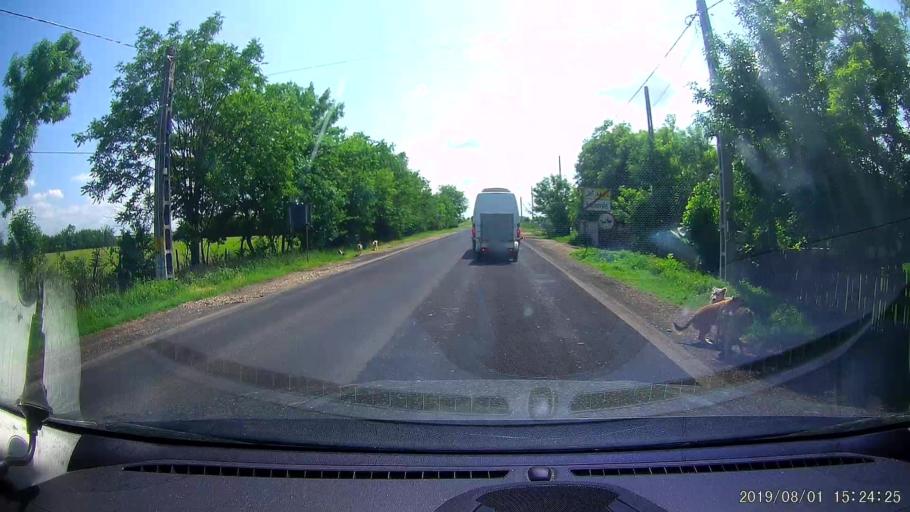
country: RO
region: Braila
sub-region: Comuna Viziru
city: Lanurile
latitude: 45.0332
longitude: 27.7496
